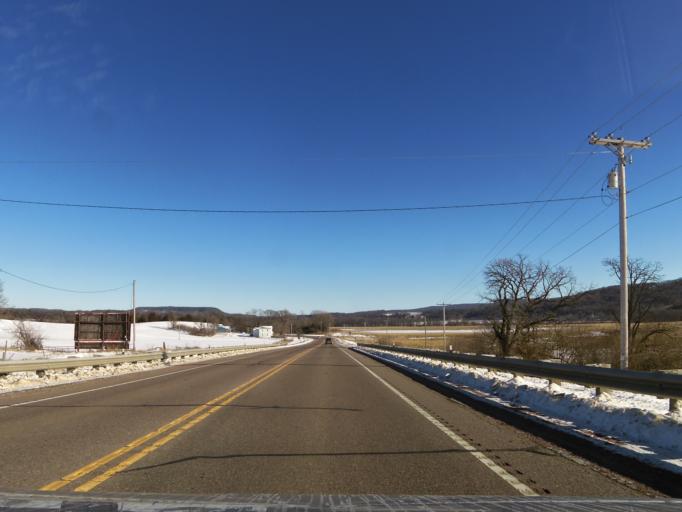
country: US
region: Wisconsin
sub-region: Sauk County
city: Baraboo
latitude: 43.4743
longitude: -89.6617
